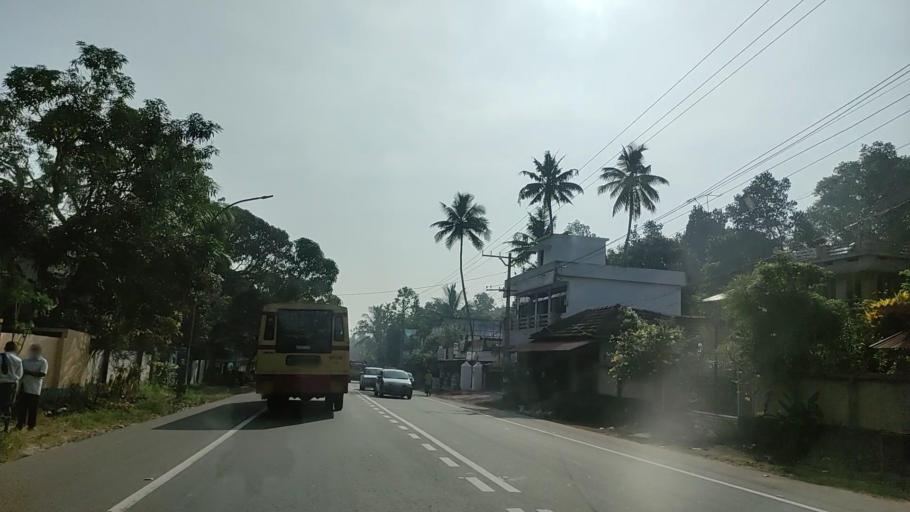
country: IN
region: Kerala
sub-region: Kollam
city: Punalur
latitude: 8.9847
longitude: 76.8041
